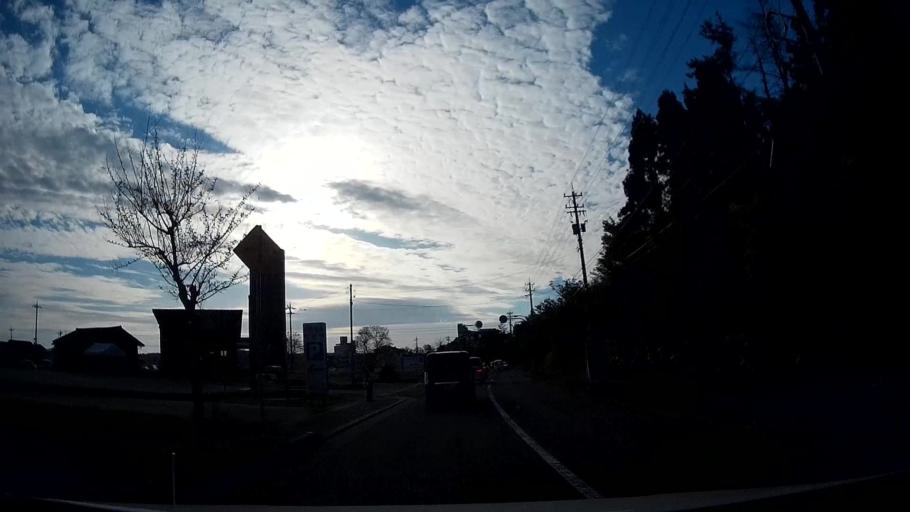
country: JP
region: Ishikawa
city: Nanao
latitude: 37.0835
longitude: 136.9333
